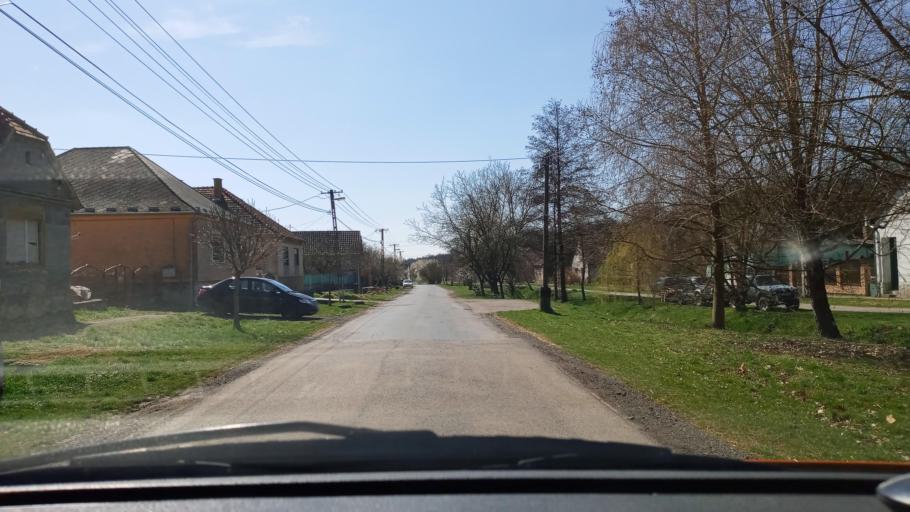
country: HU
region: Baranya
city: Pecsvarad
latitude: 46.0659
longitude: 18.4494
